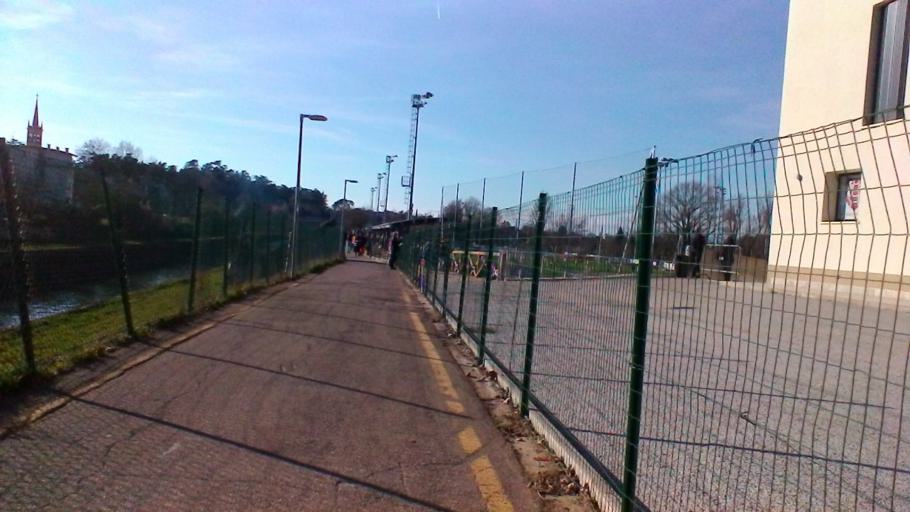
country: IT
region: Veneto
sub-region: Provincia di Verona
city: Parona
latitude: 45.4583
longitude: 10.9516
